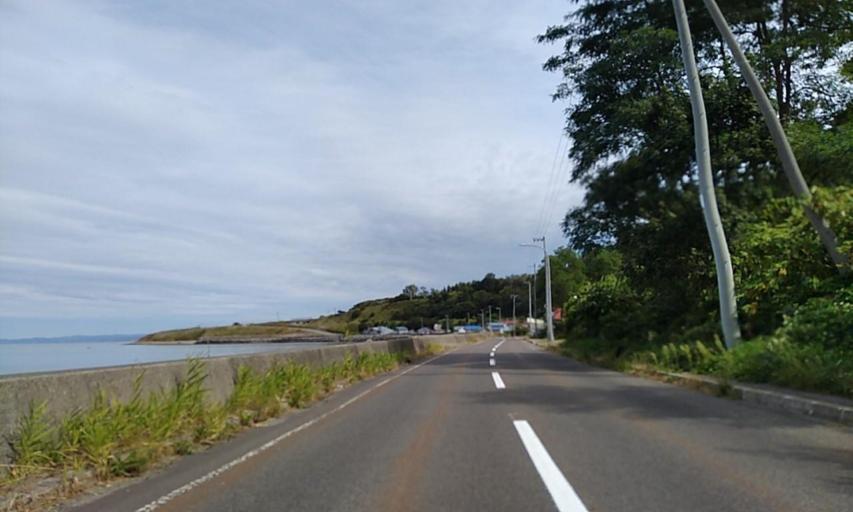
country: JP
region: Hokkaido
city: Rumoi
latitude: 43.8525
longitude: 141.5396
